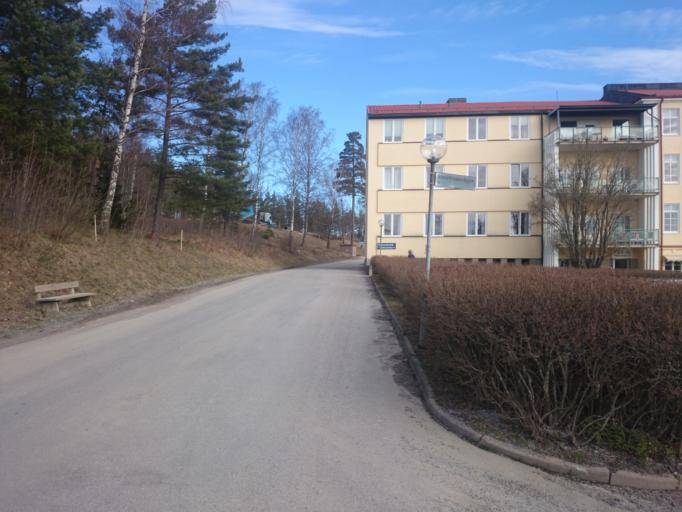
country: SE
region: Stockholm
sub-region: Botkyrka Kommun
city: Tumba
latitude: 59.2009
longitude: 17.8029
